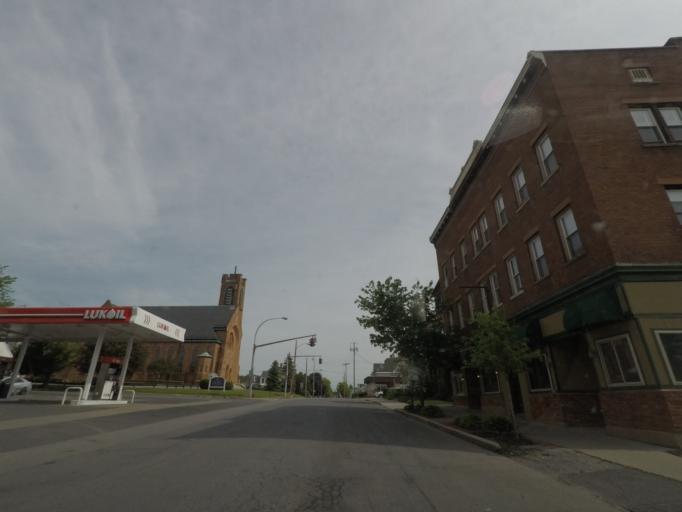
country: US
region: New York
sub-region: Saratoga County
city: Mechanicville
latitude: 42.9055
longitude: -73.6845
